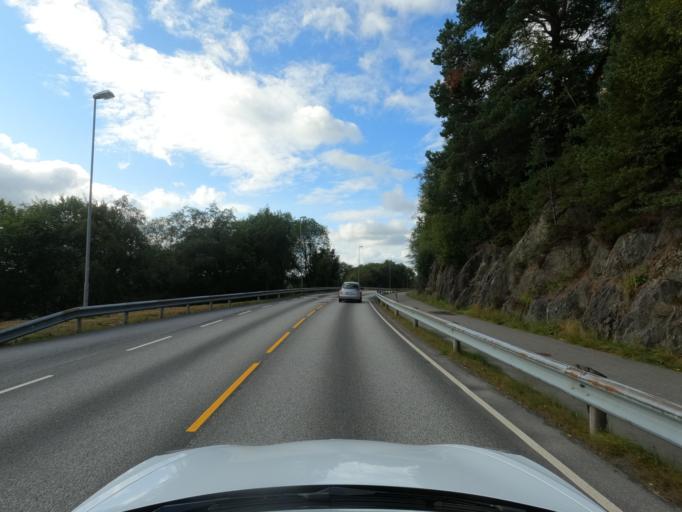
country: NO
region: Hordaland
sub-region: Bergen
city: Bergen
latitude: 60.3360
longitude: 5.3864
